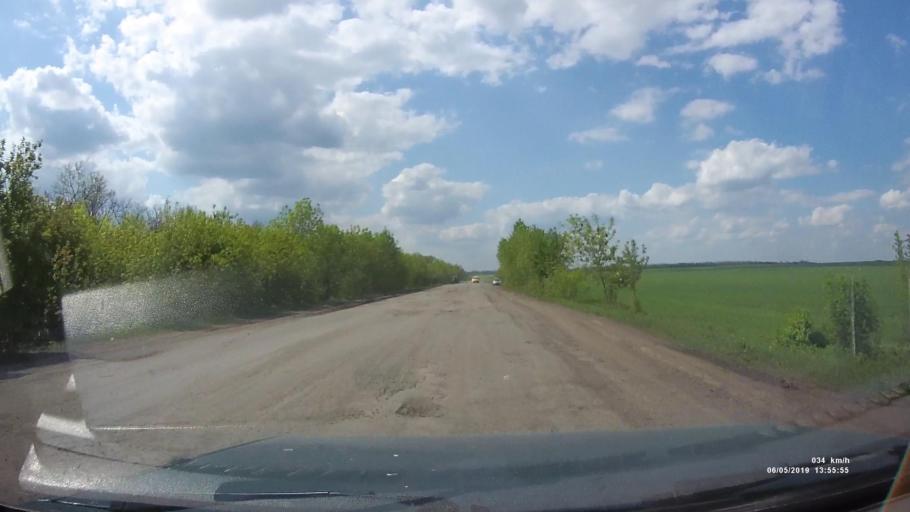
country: RU
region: Rostov
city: Melikhovskaya
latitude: 47.6795
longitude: 40.4351
